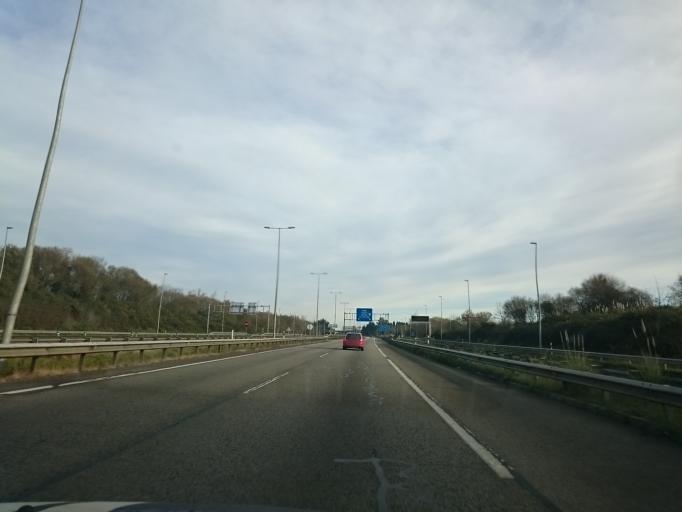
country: ES
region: Asturias
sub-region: Province of Asturias
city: Lugones
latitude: 43.4001
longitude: -5.7990
